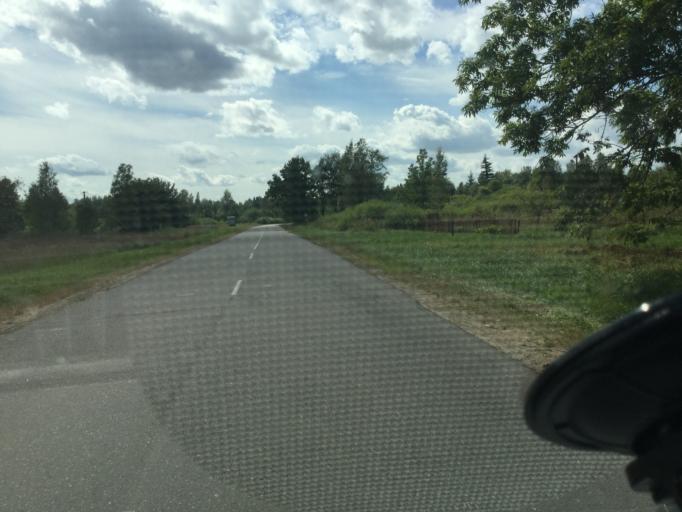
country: BY
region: Vitebsk
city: Chashniki
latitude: 55.2891
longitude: 29.3636
